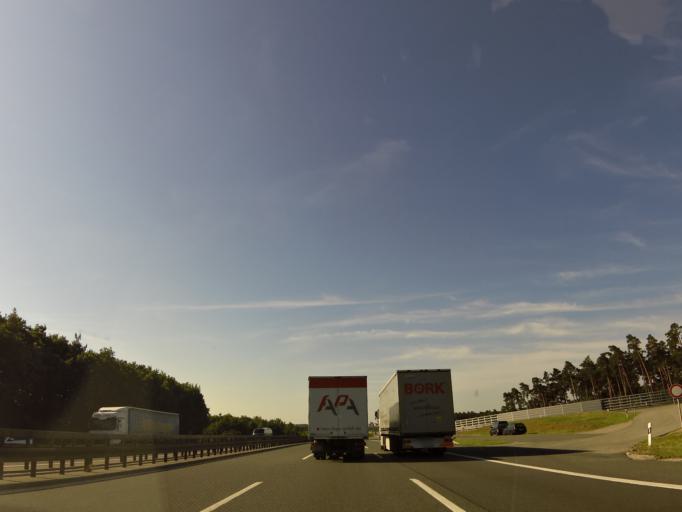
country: DE
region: Bavaria
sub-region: Regierungsbezirk Mittelfranken
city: Allersberg
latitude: 49.2525
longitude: 11.2157
